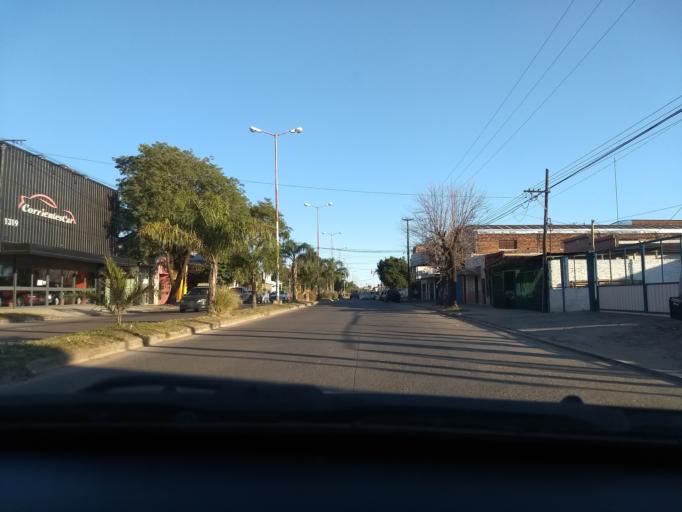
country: AR
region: Corrientes
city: Corrientes
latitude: -27.4744
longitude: -58.8137
